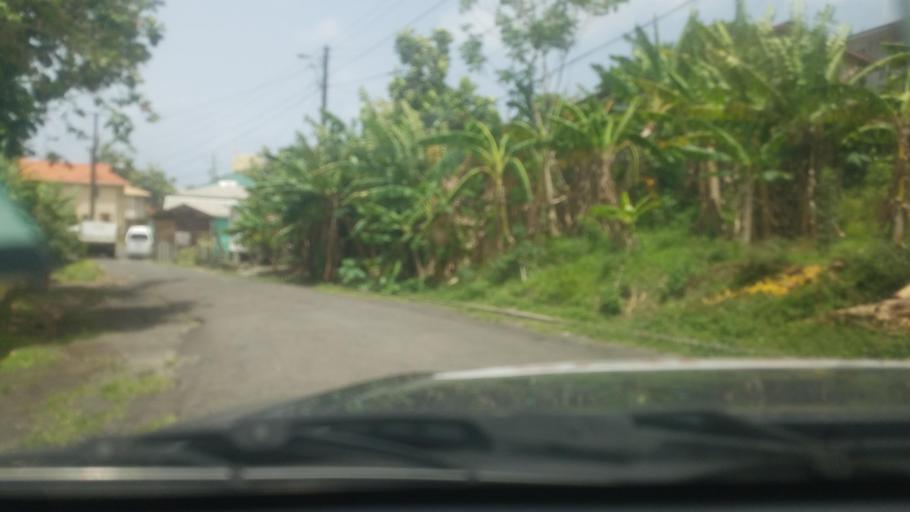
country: LC
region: Laborie Quarter
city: Laborie
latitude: 13.7514
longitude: -60.9943
